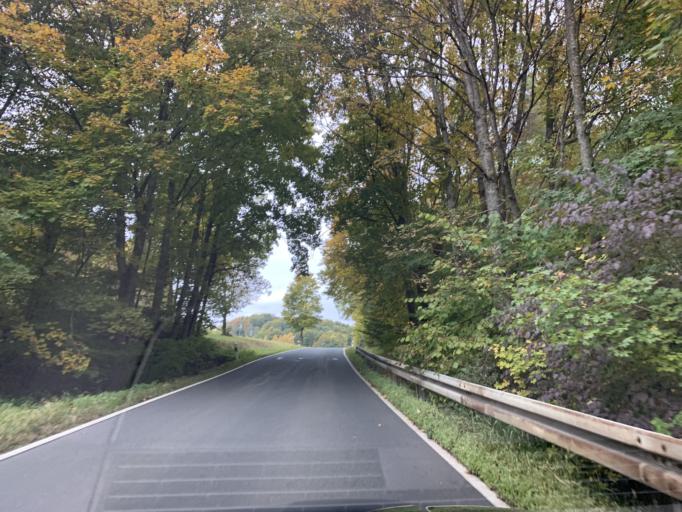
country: DE
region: Bavaria
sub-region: Upper Franconia
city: Gossweinstein
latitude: 49.7820
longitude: 11.3209
